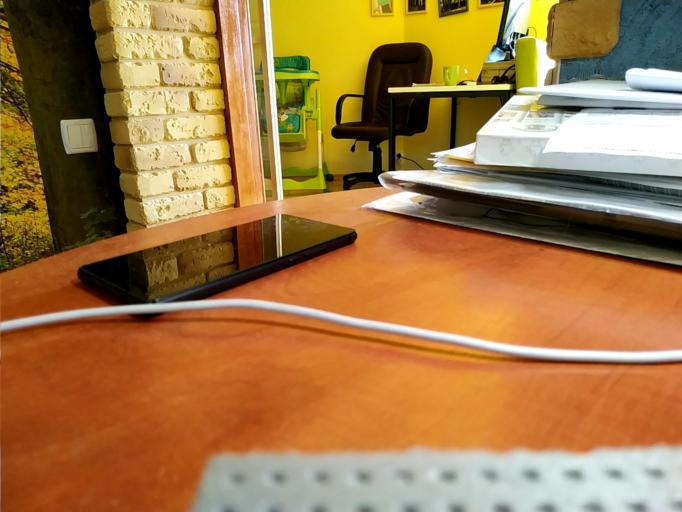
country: RU
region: Tverskaya
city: Kalashnikovo
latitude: 57.3872
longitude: 35.3121
